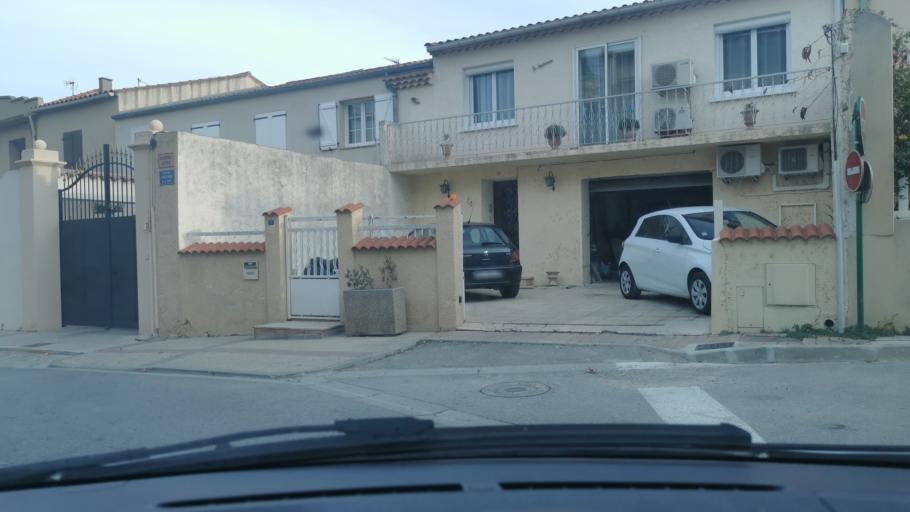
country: FR
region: Languedoc-Roussillon
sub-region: Departement de l'Herault
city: Mireval
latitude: 43.5077
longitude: 3.8018
